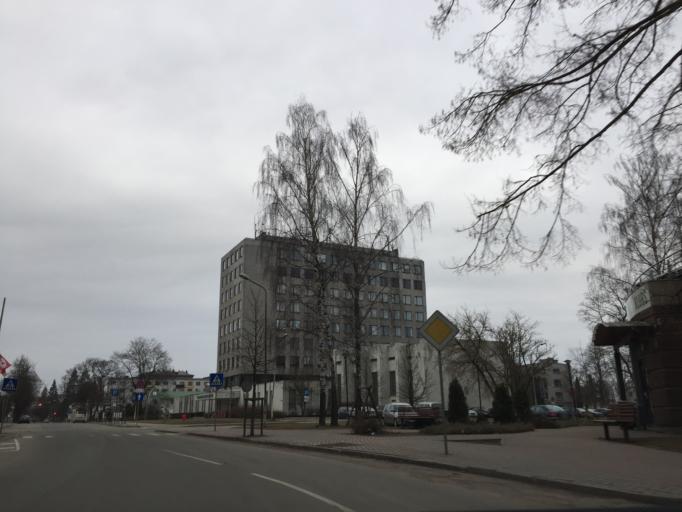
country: LV
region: Jelgava
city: Jelgava
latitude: 56.6469
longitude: 23.7306
